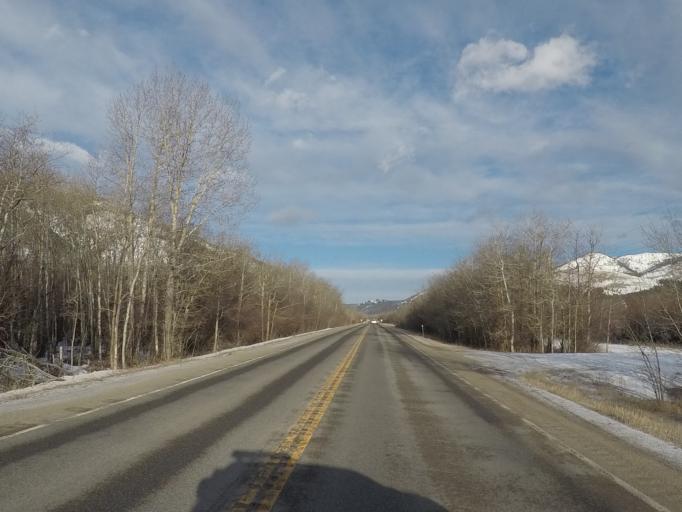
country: US
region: Montana
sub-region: Deer Lodge County
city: Anaconda
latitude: 46.1537
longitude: -113.0311
